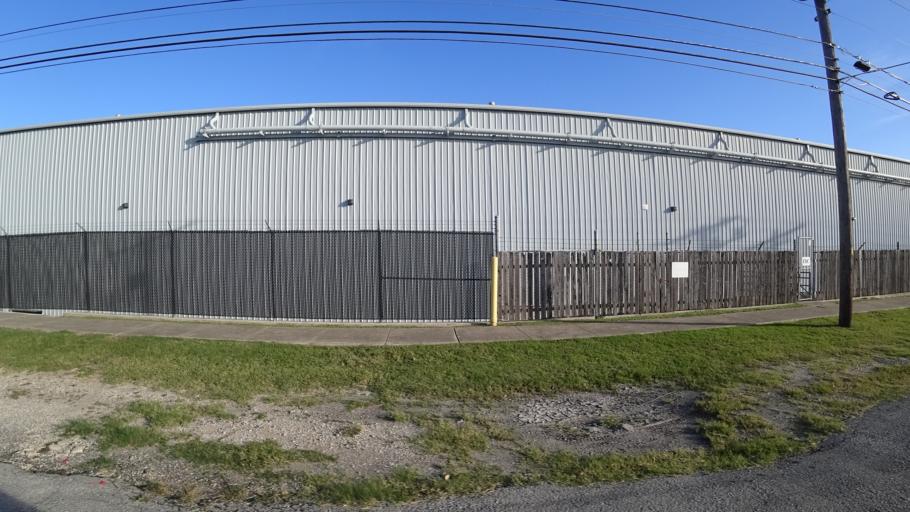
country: US
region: Texas
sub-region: Williamson County
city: Jollyville
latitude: 30.3799
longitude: -97.7270
